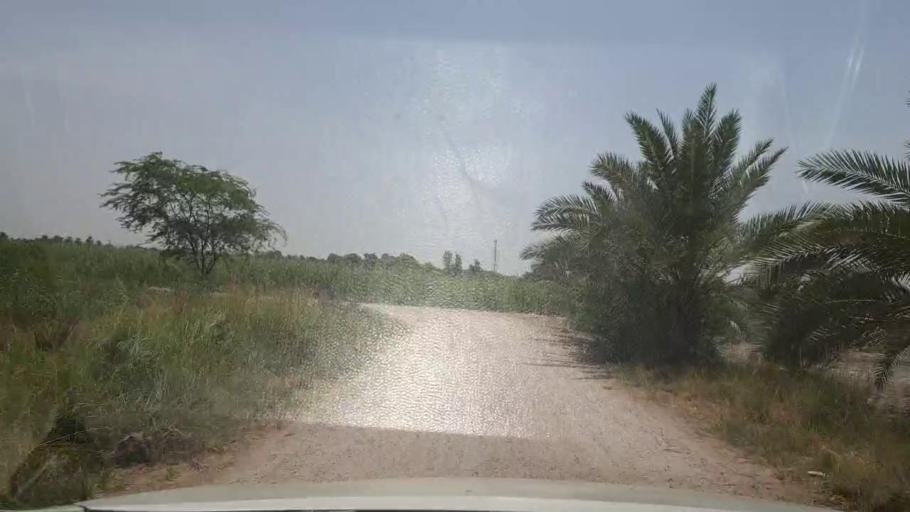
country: PK
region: Sindh
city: Bozdar
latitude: 27.2130
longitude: 68.6617
